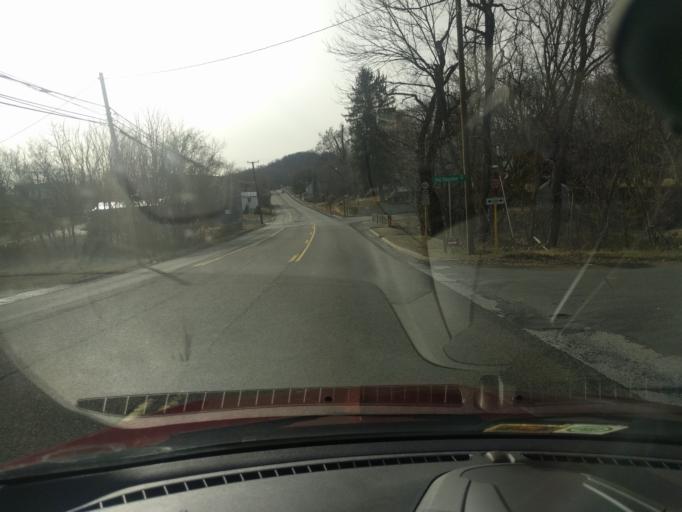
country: US
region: Virginia
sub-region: Augusta County
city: Stuarts Draft
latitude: 38.0056
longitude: -79.1551
